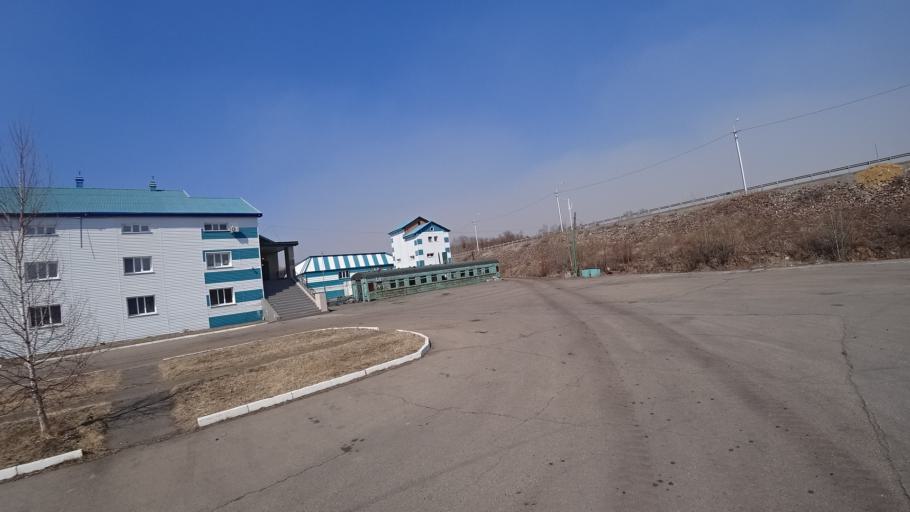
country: RU
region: Amur
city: Novobureyskiy
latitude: 49.7862
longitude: 129.9373
